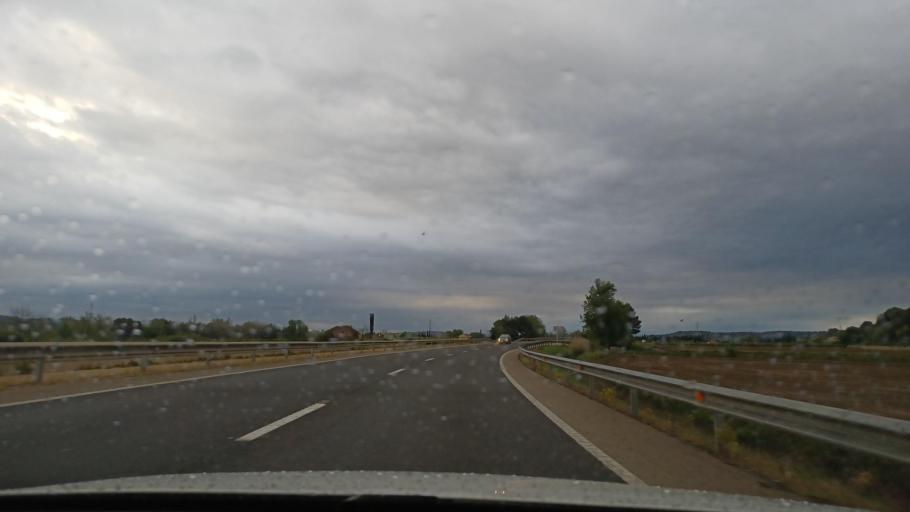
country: ES
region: Catalonia
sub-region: Provincia de Tarragona
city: Tortosa
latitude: 40.7745
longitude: 0.5260
